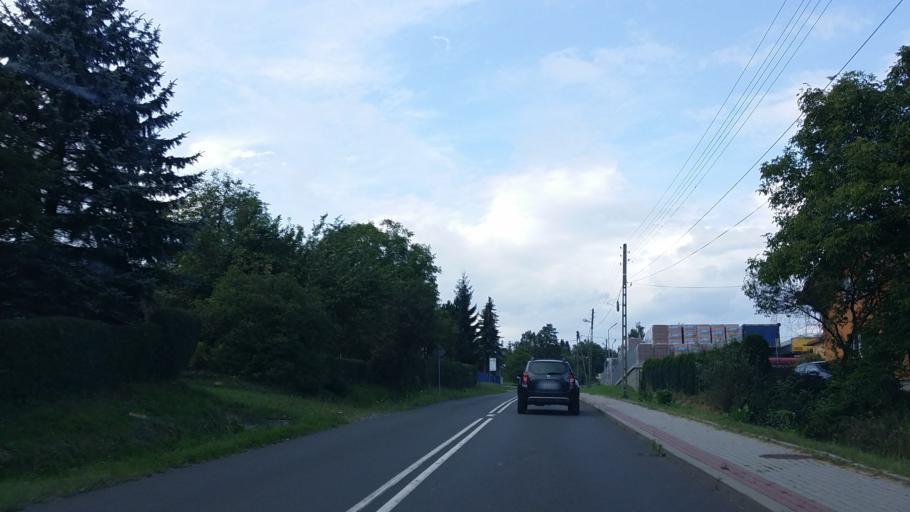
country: PL
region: Lesser Poland Voivodeship
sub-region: Powiat wielicki
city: Pawlikowice
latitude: 49.9671
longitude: 20.0428
